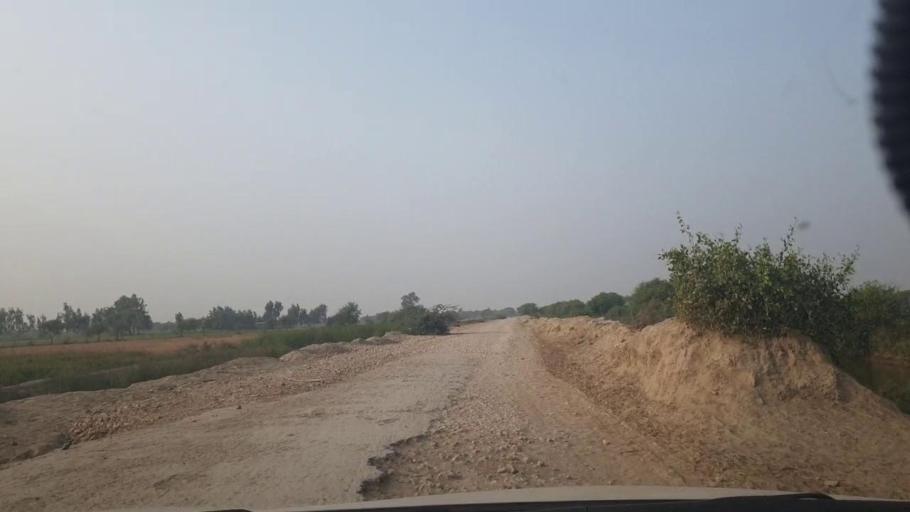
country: PK
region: Sindh
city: Bulri
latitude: 24.7971
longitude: 68.4156
